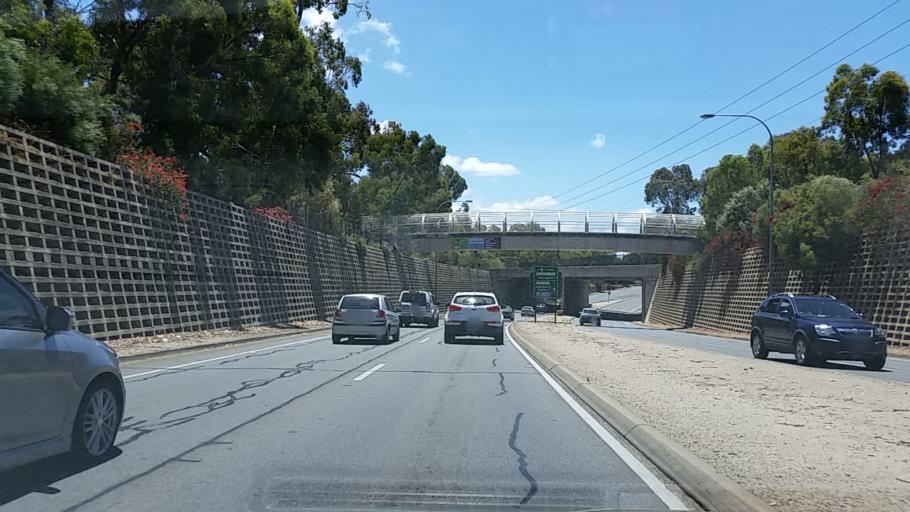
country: AU
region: South Australia
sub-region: Salisbury
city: Salisbury
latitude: -34.7613
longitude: 138.6417
